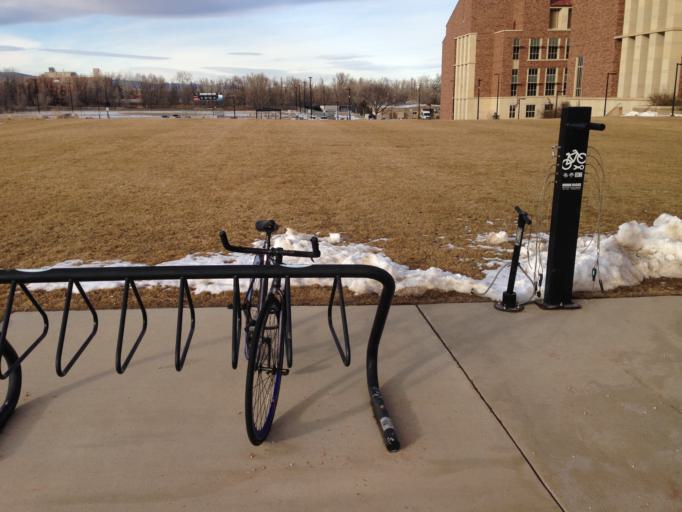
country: US
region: Colorado
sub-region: Boulder County
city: Boulder
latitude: 40.0080
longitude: -105.2499
